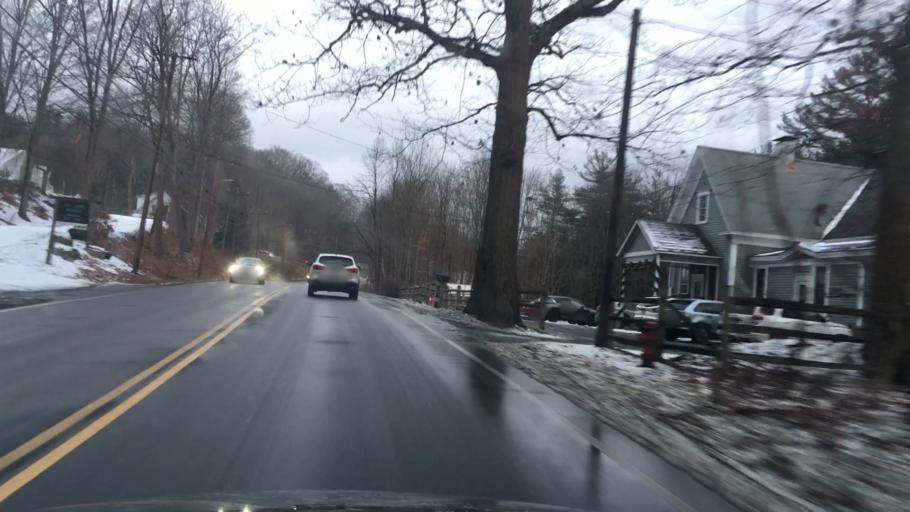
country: US
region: New Hampshire
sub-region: Sullivan County
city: Claremont
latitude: 43.3920
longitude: -72.3725
